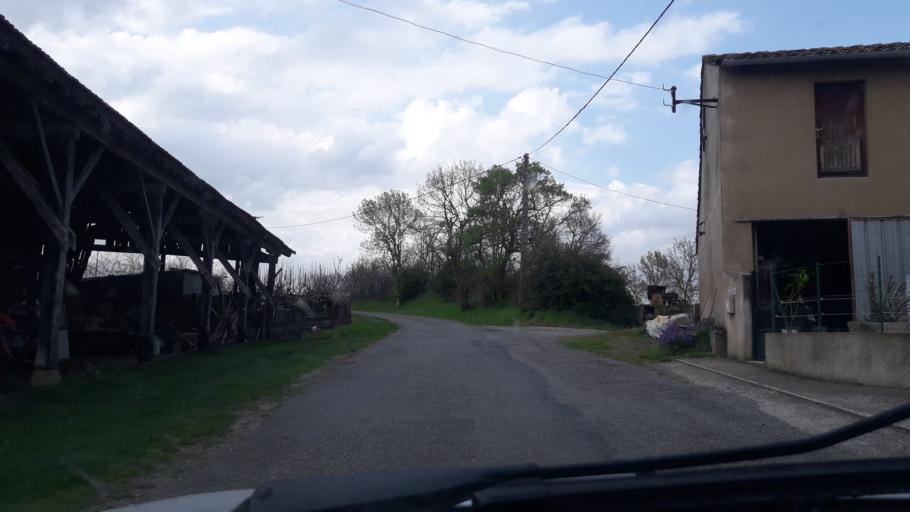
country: FR
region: Midi-Pyrenees
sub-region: Departement de l'Ariege
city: Lezat-sur-Leze
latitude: 43.1932
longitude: 1.3271
